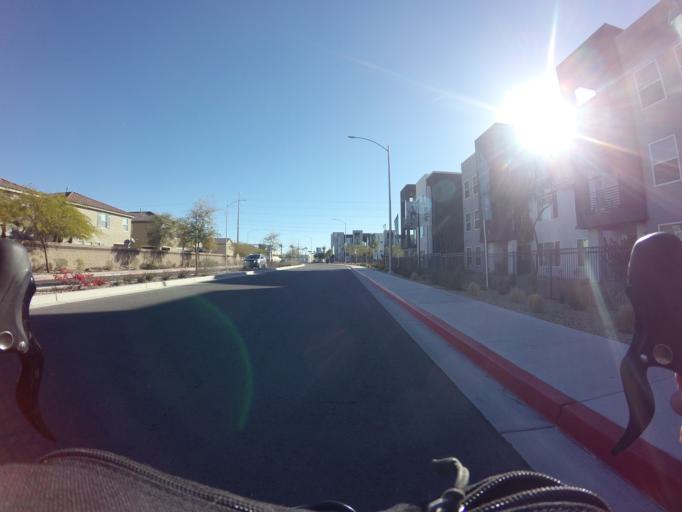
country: US
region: Nevada
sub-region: Clark County
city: Whitney
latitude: 36.0368
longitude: -115.0486
